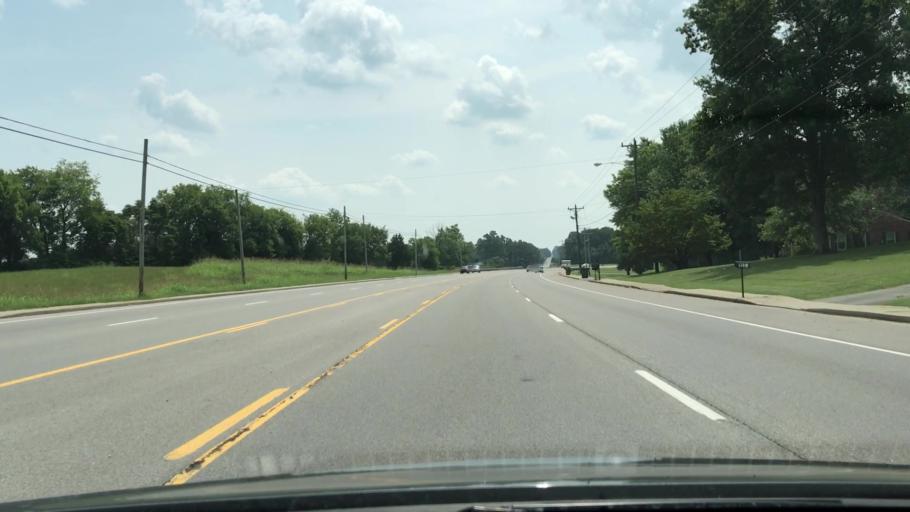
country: US
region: Tennessee
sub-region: Sumner County
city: Portland
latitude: 36.5465
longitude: -86.5057
